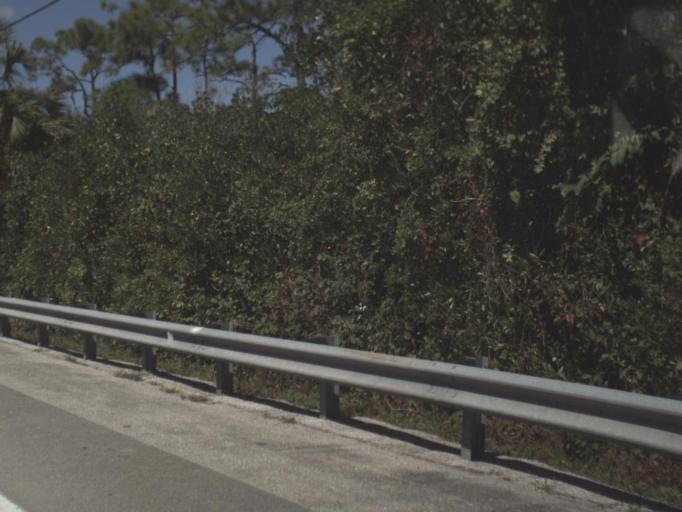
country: US
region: Florida
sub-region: Collier County
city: Lely Resort
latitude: 25.9873
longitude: -81.5737
